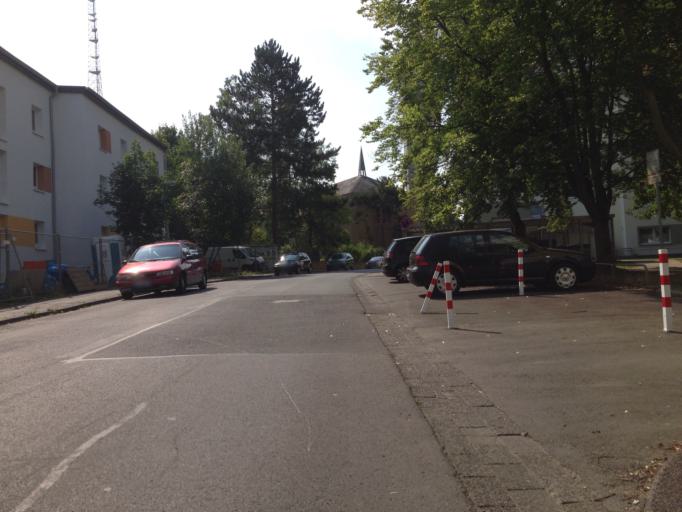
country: DE
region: Hesse
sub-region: Regierungsbezirk Giessen
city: Giessen
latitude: 50.5908
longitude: 8.7029
